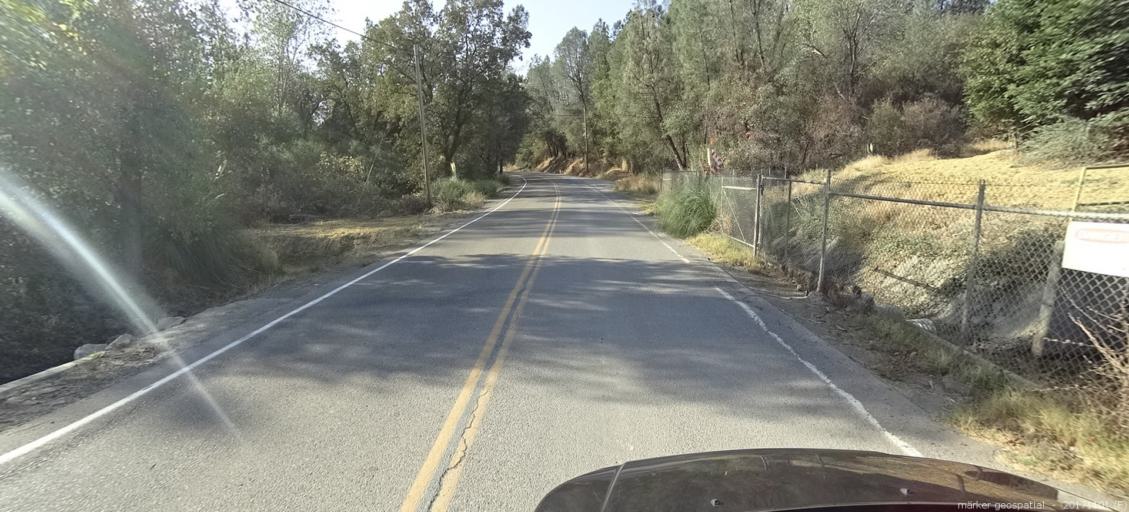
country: US
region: California
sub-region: Shasta County
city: Shasta Lake
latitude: 40.7339
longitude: -122.3217
